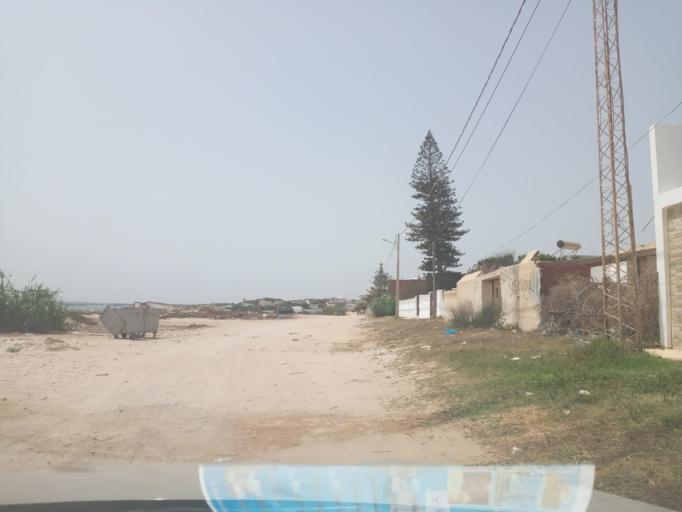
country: TN
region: Nabul
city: El Haouaria
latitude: 37.0339
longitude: 11.0582
